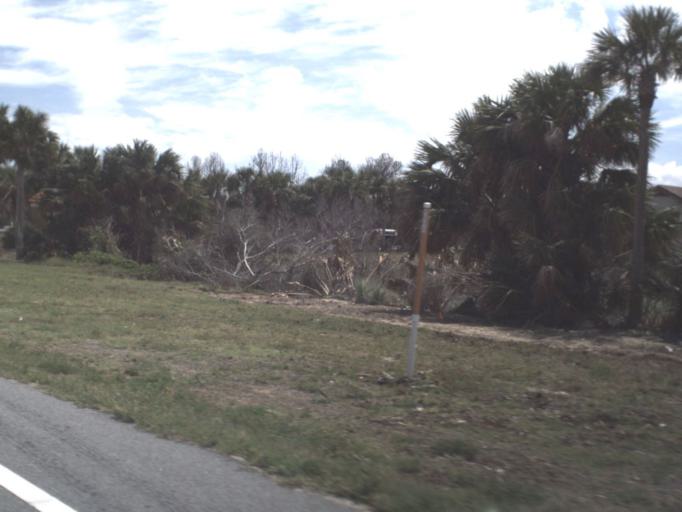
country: US
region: Florida
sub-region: Flagler County
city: Palm Coast
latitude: 29.6471
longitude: -81.2061
